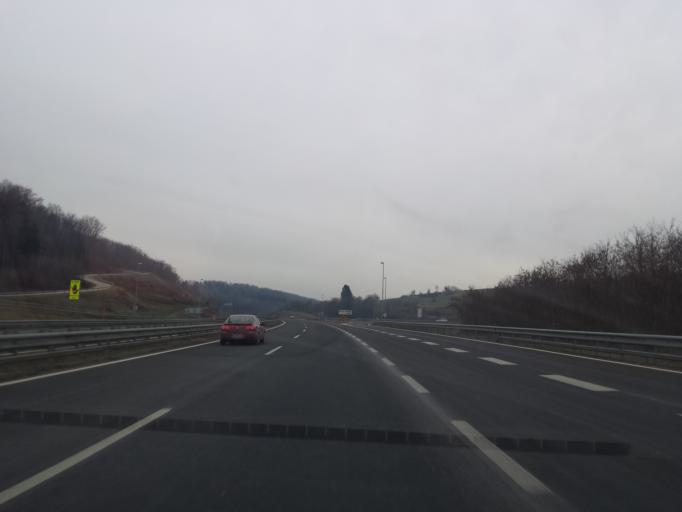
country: SI
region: Novo Mesto
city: Novo Mesto
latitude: 45.8419
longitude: 15.1569
